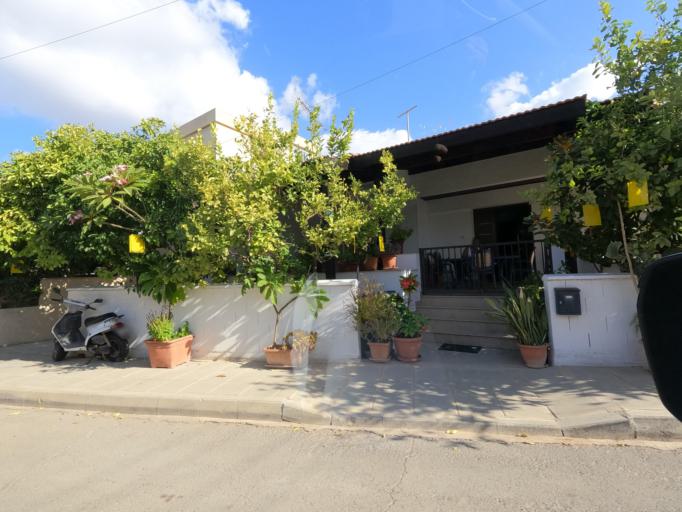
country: CY
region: Pafos
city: Paphos
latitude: 34.7827
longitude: 32.4345
